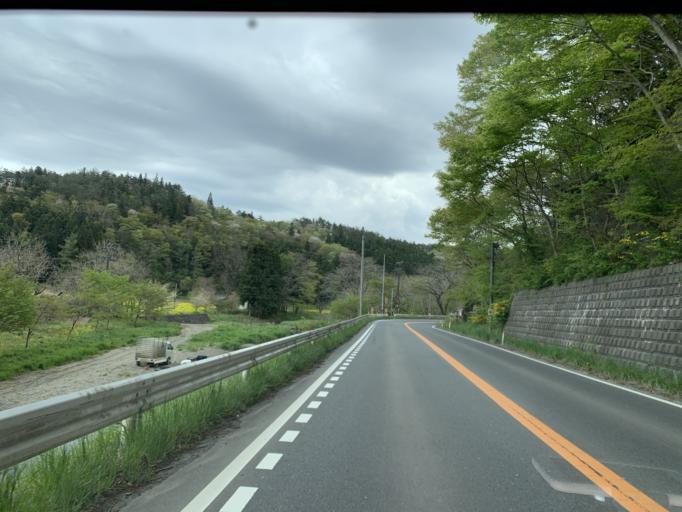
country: JP
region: Iwate
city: Ichinoseki
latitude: 38.7829
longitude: 141.3895
